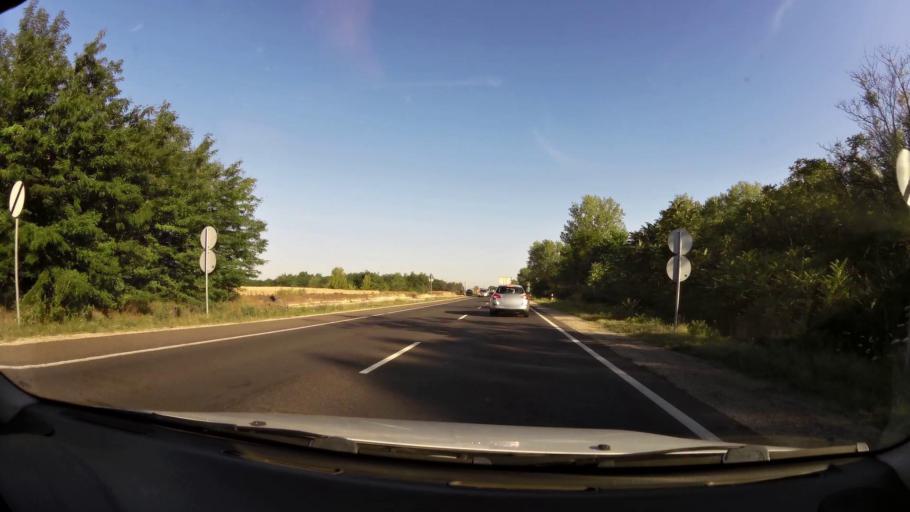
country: HU
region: Pest
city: Cegledbercel
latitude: 47.2454
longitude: 19.6516
